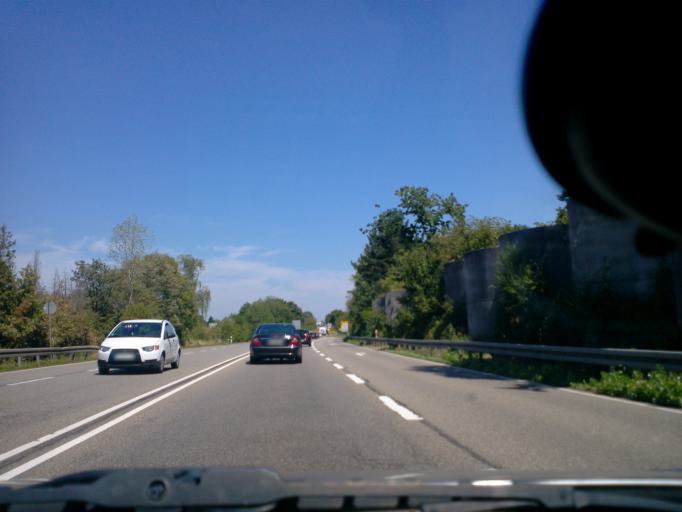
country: DE
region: Baden-Wuerttemberg
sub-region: Freiburg Region
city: Offenburg
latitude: 48.4542
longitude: 7.9316
